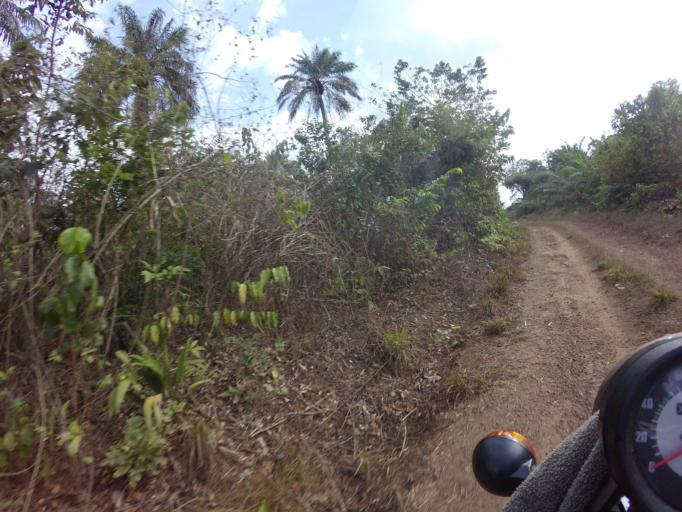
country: SL
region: Southern Province
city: Zimmi
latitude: 7.1497
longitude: -11.1965
